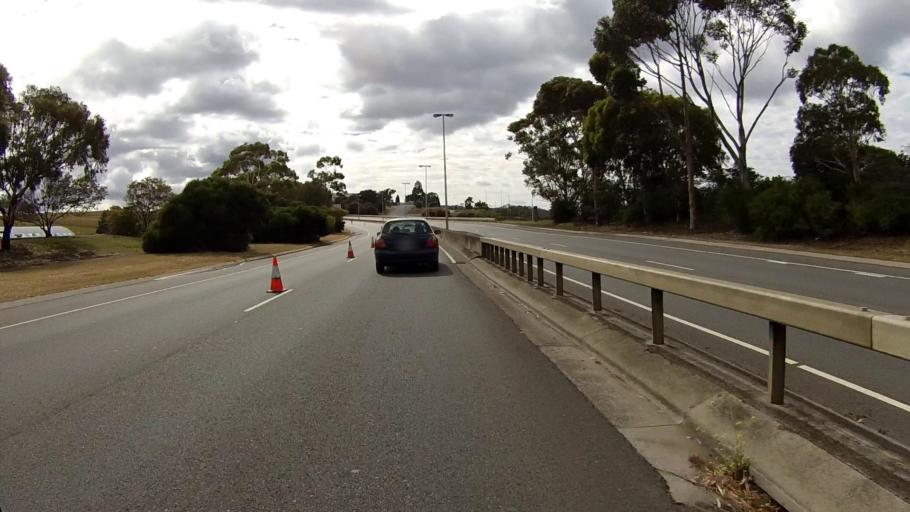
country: AU
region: Tasmania
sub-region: Glenorchy
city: Goodwood
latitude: -42.8233
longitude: 147.2966
